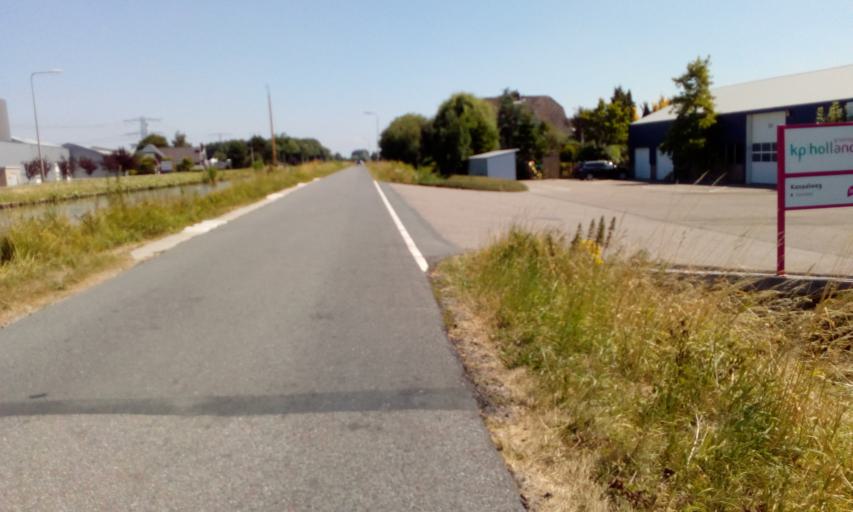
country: NL
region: South Holland
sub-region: Gemeente Westland
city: De Lier
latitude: 51.9850
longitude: 4.2413
